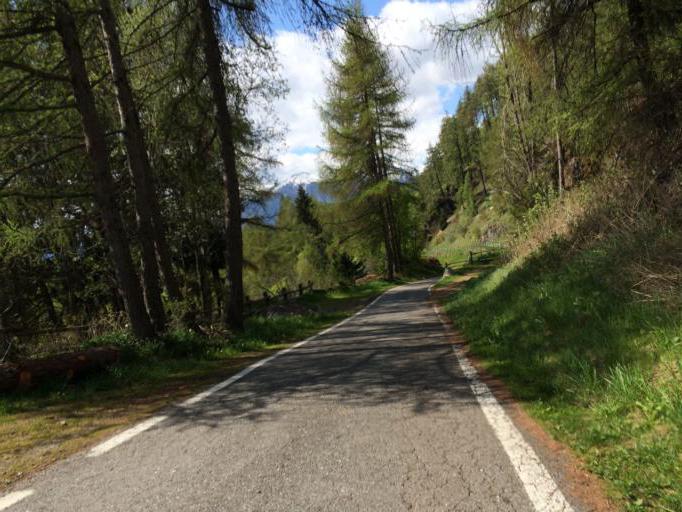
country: IT
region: Trentino-Alto Adige
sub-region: Bolzano
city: Malles Venosta
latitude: 46.7338
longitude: 10.5323
